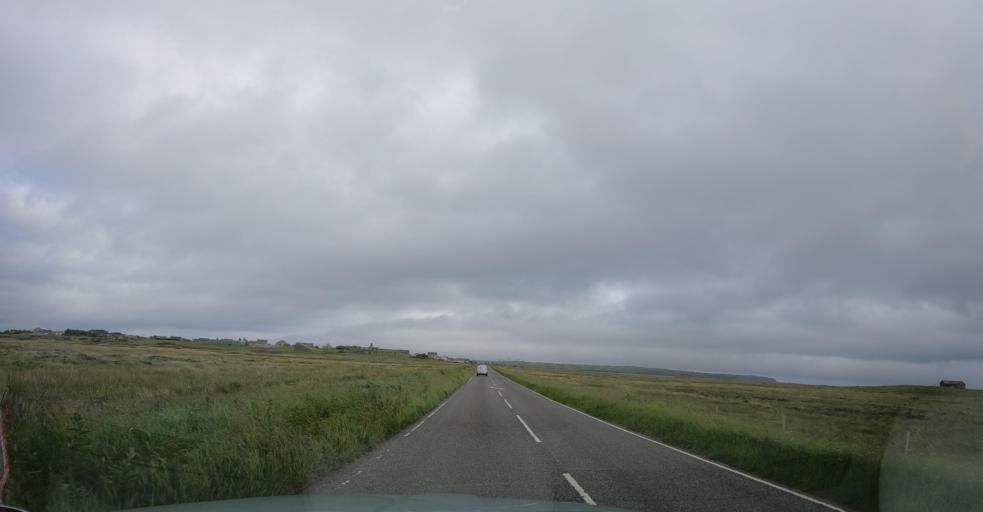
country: GB
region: Scotland
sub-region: Eilean Siar
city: Stornoway
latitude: 58.2035
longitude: -6.3276
